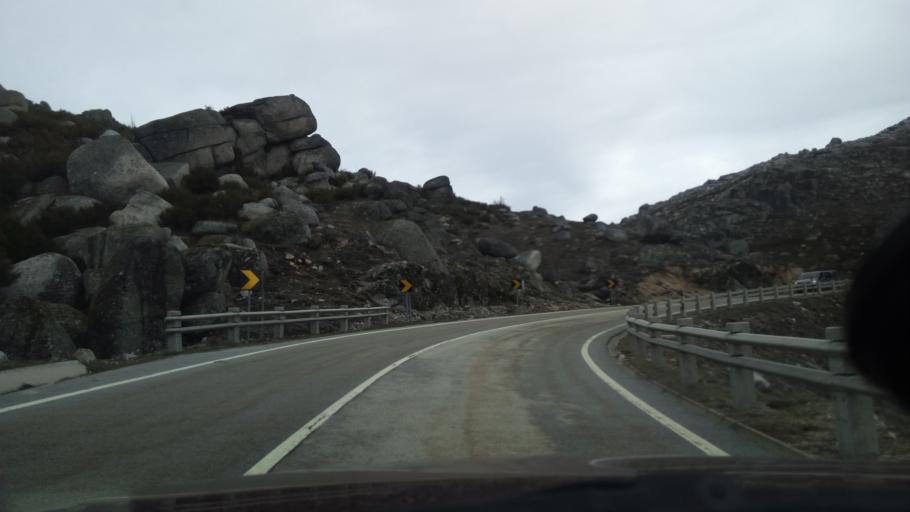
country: PT
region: Guarda
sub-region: Seia
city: Seia
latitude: 40.3561
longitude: -7.6790
